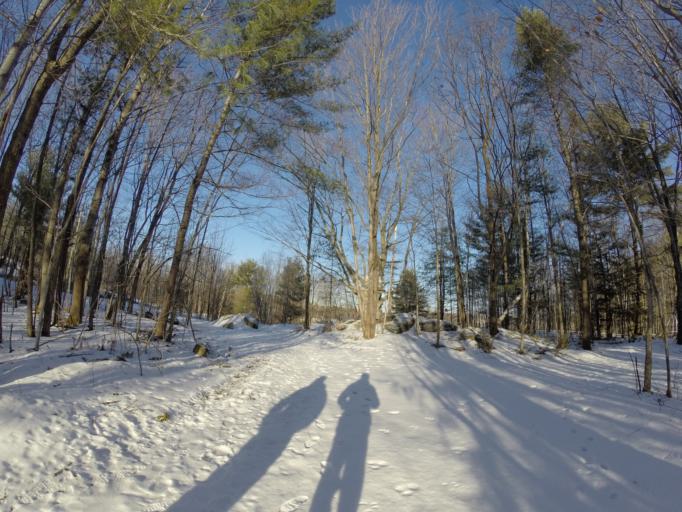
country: CA
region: Ontario
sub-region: Parry Sound District
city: Parry Sound
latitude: 45.3602
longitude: -80.0304
